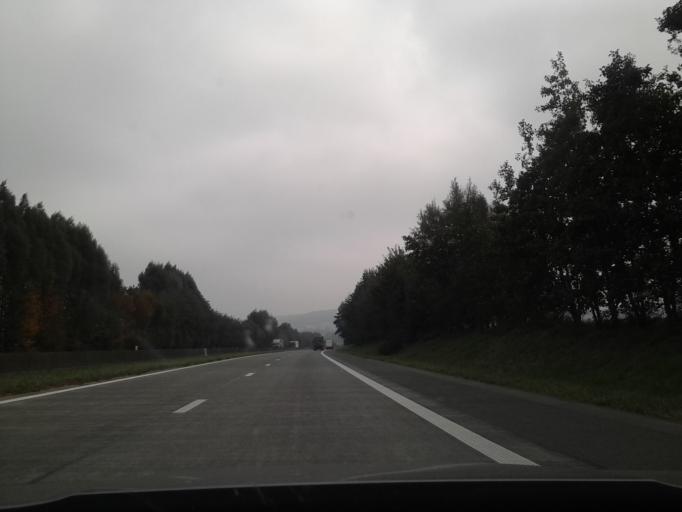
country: BE
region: Wallonia
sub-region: Province du Hainaut
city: Frasnes-lez-Buissenal
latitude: 50.6603
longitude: 3.6328
